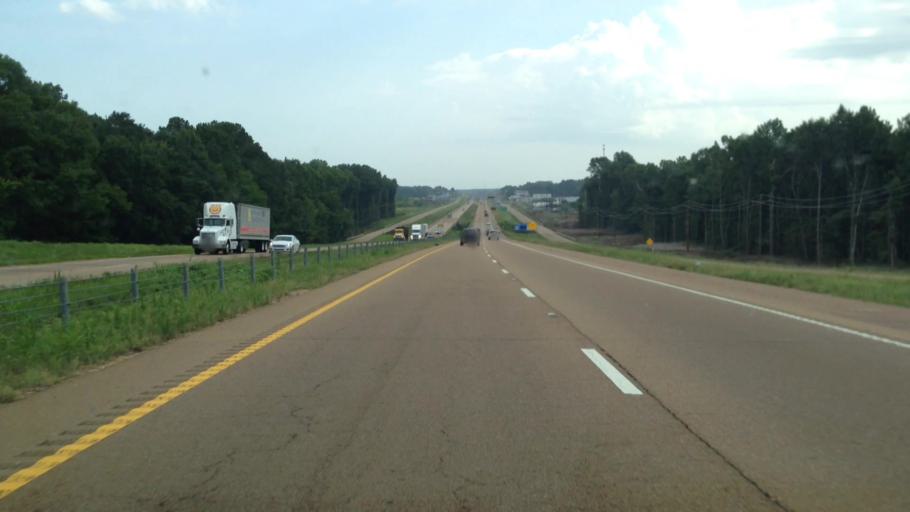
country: US
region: Mississippi
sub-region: Hinds County
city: Byram
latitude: 32.1605
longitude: -90.2723
